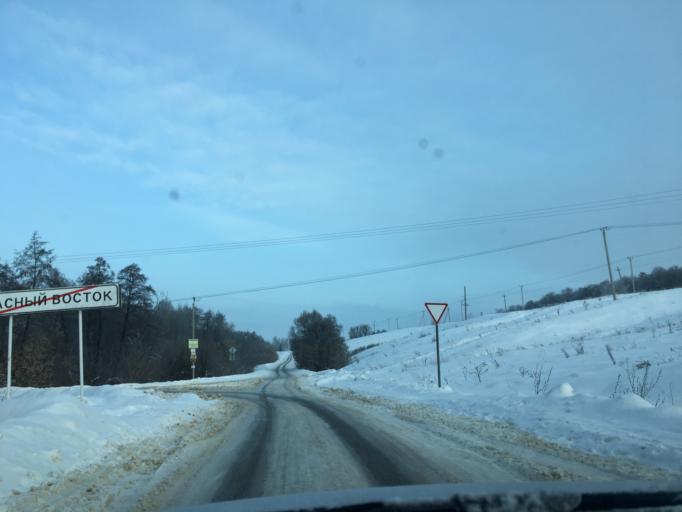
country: RU
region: Belgorod
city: Severnyy
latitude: 50.7266
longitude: 36.6120
